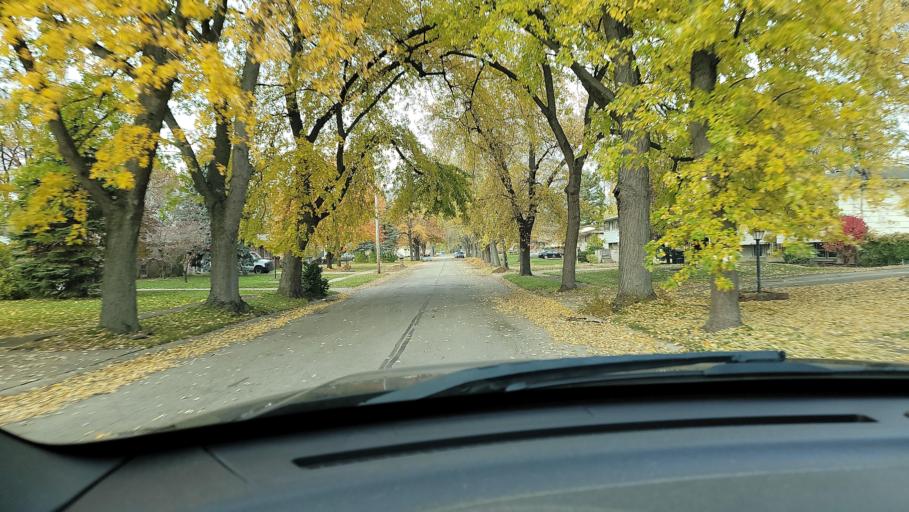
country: US
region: Indiana
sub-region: Porter County
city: Portage
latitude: 41.5947
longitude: -87.1579
